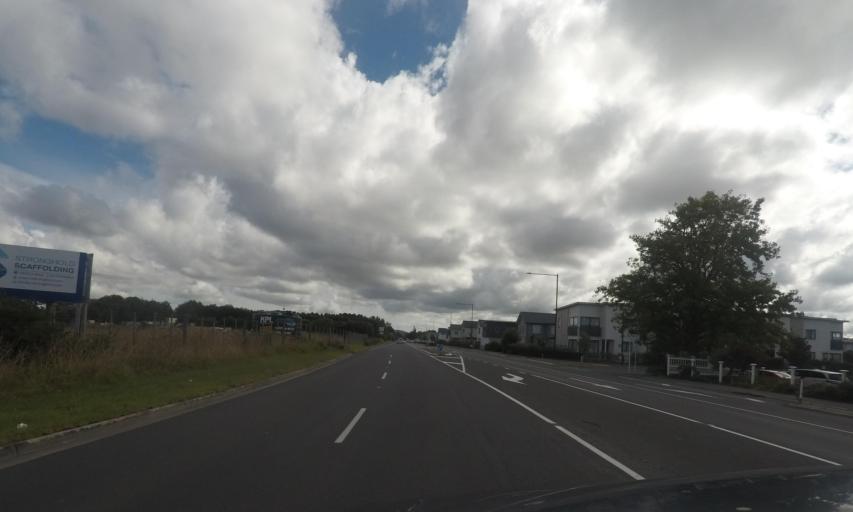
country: NZ
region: Auckland
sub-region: Auckland
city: Rosebank
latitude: -36.7927
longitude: 174.6127
